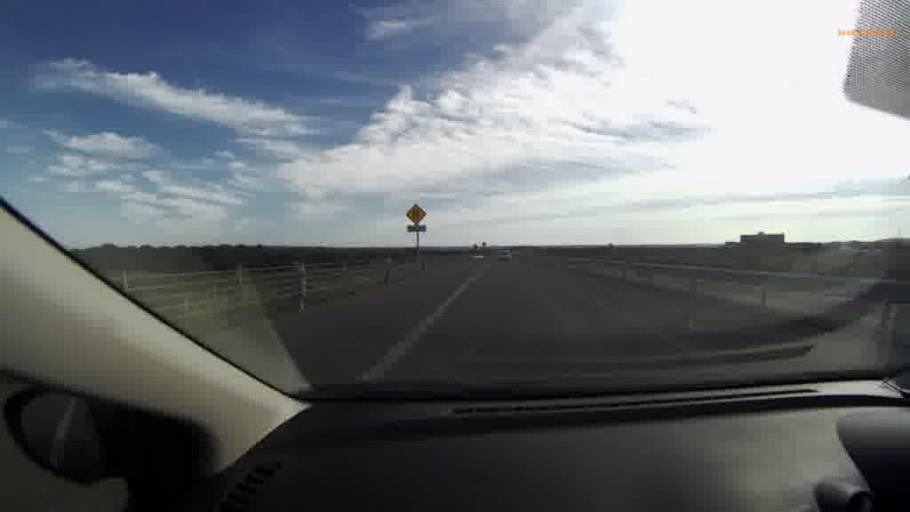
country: JP
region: Hokkaido
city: Kushiro
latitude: 43.0371
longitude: 144.3513
